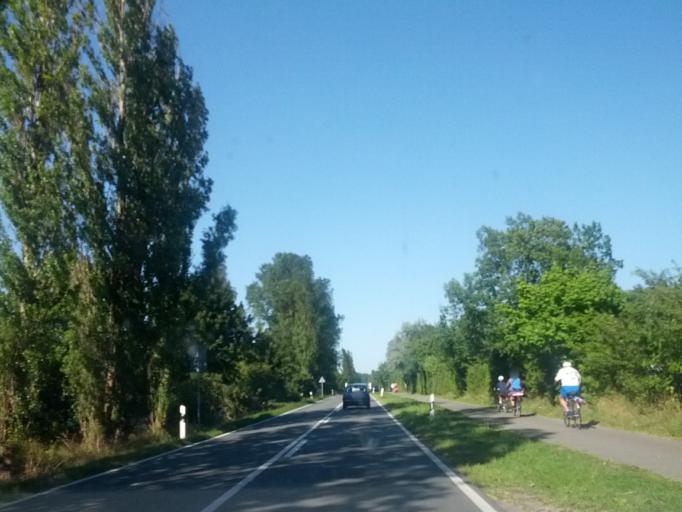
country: DE
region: Mecklenburg-Vorpommern
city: Ostseebad Gohren
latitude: 54.3114
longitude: 13.7163
